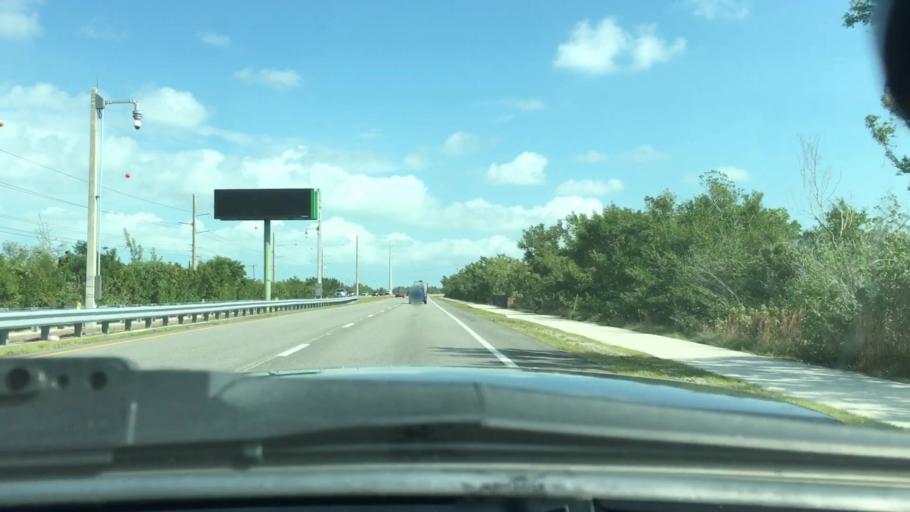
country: US
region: Florida
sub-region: Monroe County
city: Big Coppitt Key
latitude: 24.5850
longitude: -81.6986
